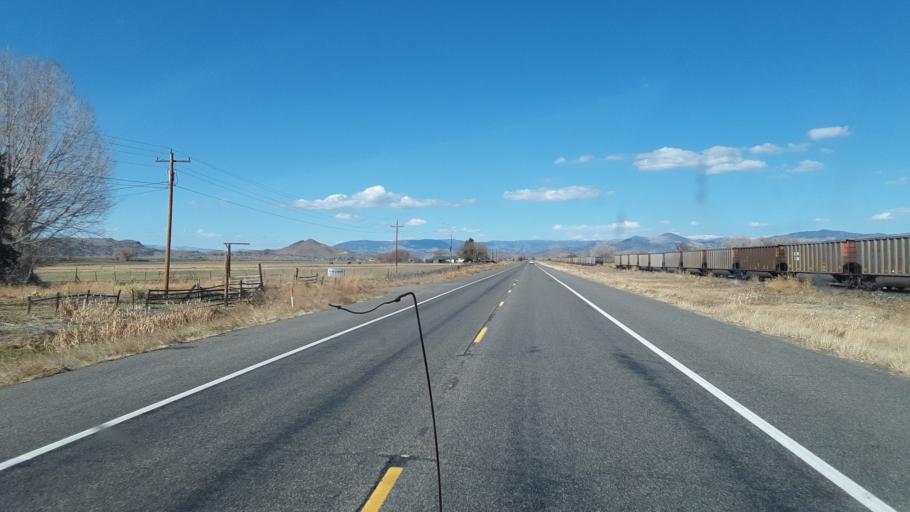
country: US
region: Colorado
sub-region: Rio Grande County
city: Del Norte
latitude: 37.6597
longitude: -106.2945
